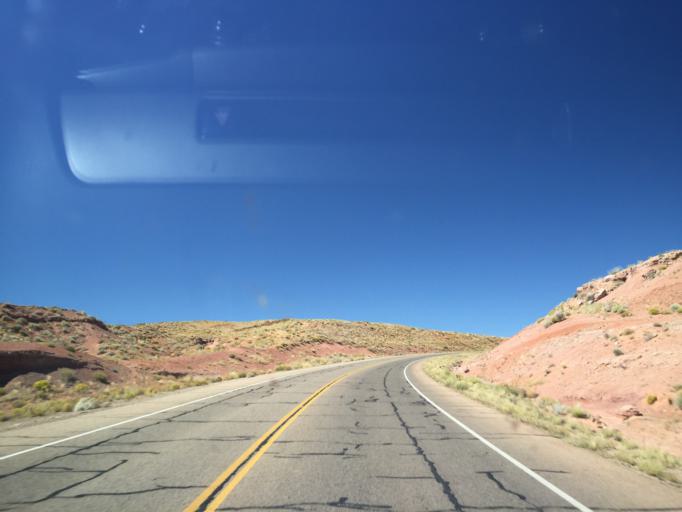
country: US
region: Arizona
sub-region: Apache County
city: Many Farms
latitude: 36.3606
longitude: -109.6398
